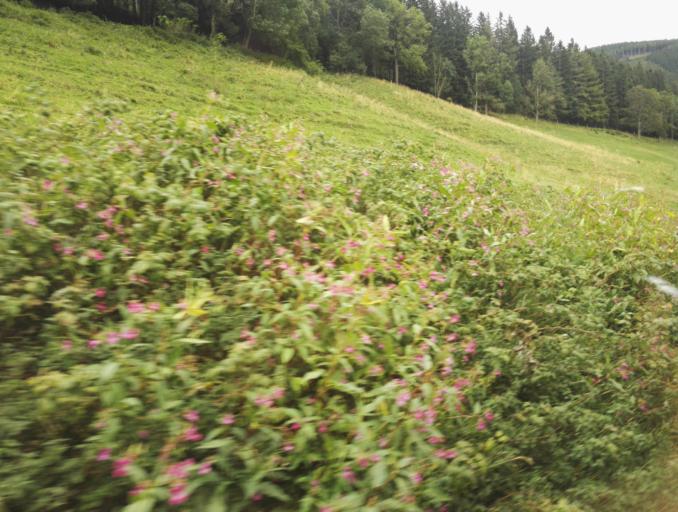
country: AT
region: Styria
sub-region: Politischer Bezirk Leoben
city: Vordernberg
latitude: 47.4920
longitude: 14.9964
